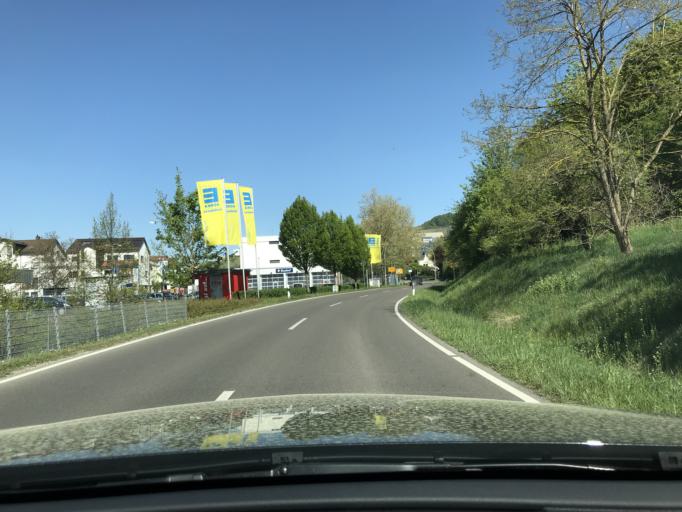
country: DE
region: Baden-Wuerttemberg
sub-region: Regierungsbezirk Stuttgart
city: Korb
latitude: 48.8359
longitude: 9.3680
